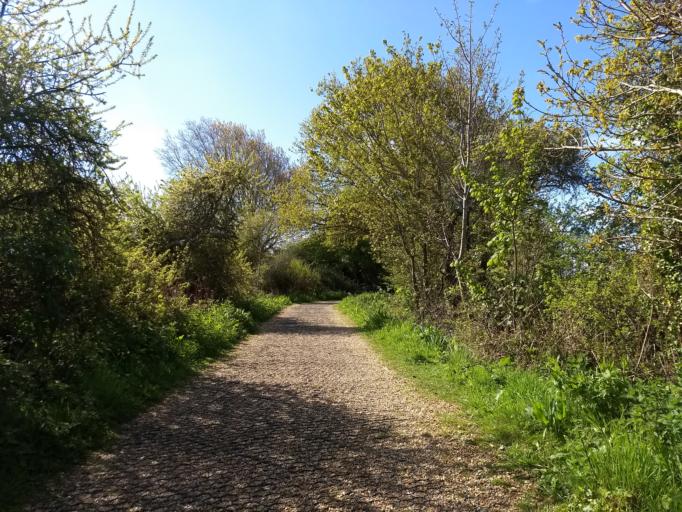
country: GB
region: England
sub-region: Isle of Wight
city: Newport
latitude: 50.7123
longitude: -1.2874
